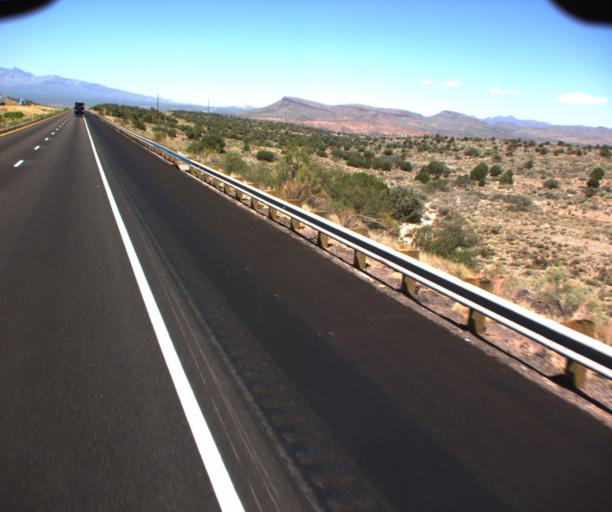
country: US
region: Arizona
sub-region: Mohave County
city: Peach Springs
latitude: 35.1621
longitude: -113.5892
